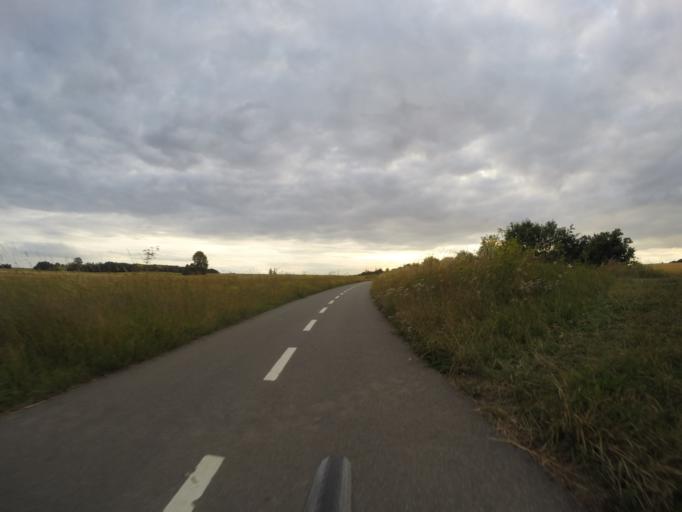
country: DK
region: Capital Region
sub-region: Hoje-Taastrup Kommune
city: Taastrup
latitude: 55.6829
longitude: 12.2808
